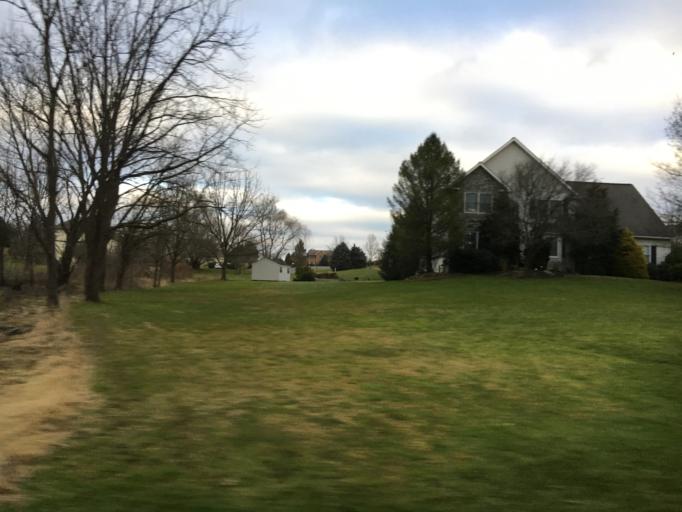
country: US
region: Pennsylvania
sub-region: Lehigh County
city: Schnecksville
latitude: 40.6908
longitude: -75.5985
